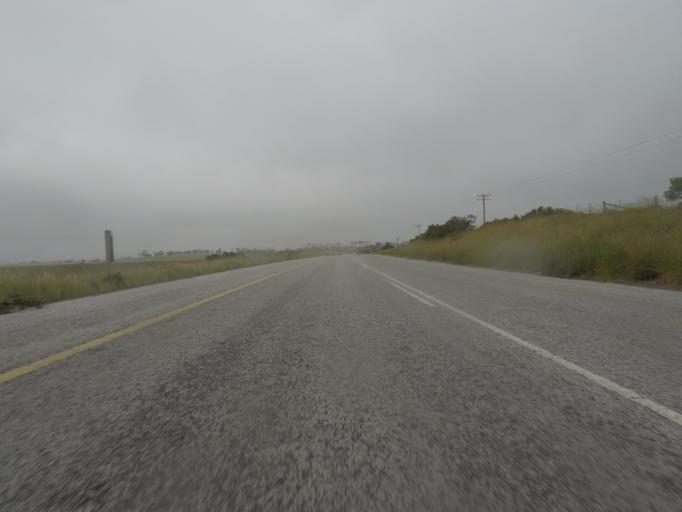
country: ZA
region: Eastern Cape
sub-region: Cacadu District Municipality
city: Grahamstown
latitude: -33.6425
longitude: 26.3376
